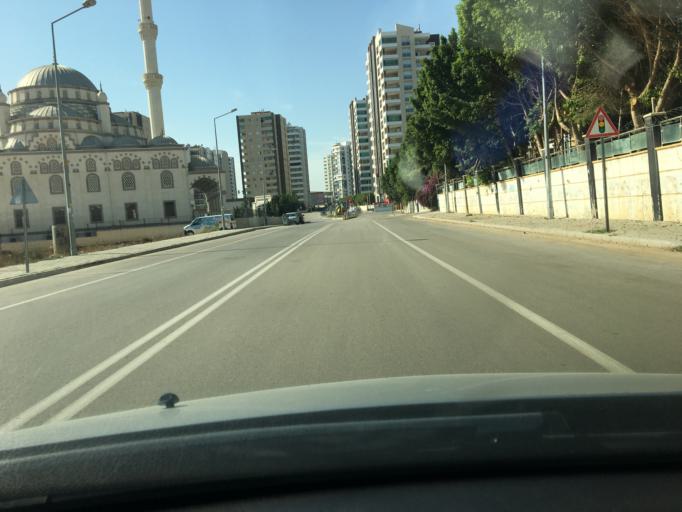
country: TR
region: Adana
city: Seyhan
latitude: 37.0196
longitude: 35.2599
